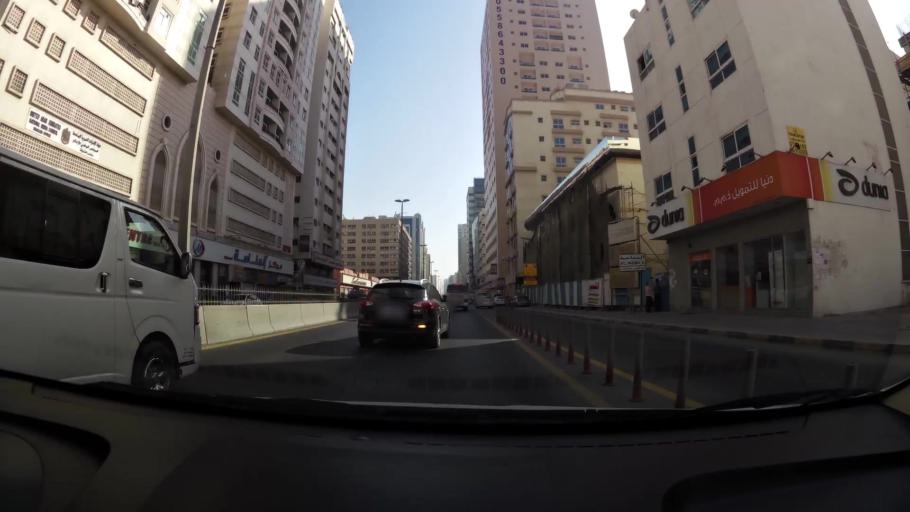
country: AE
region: Ash Shariqah
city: Sharjah
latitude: 25.3634
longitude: 55.3919
